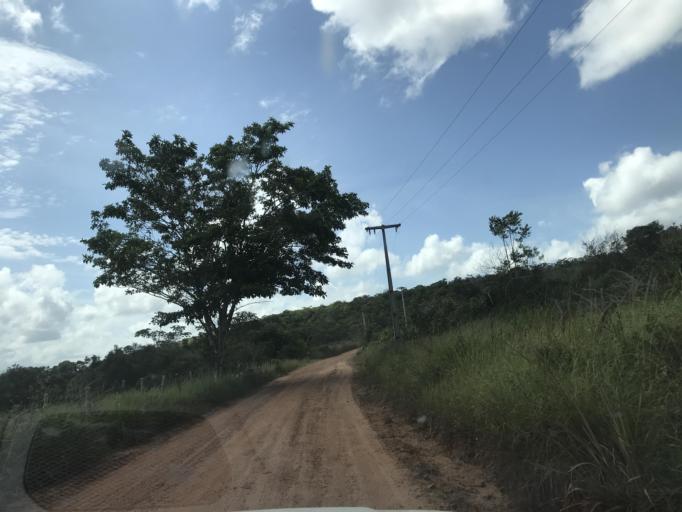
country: BR
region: Bahia
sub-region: Entre Rios
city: Entre Rios
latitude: -12.1762
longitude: -38.0622
